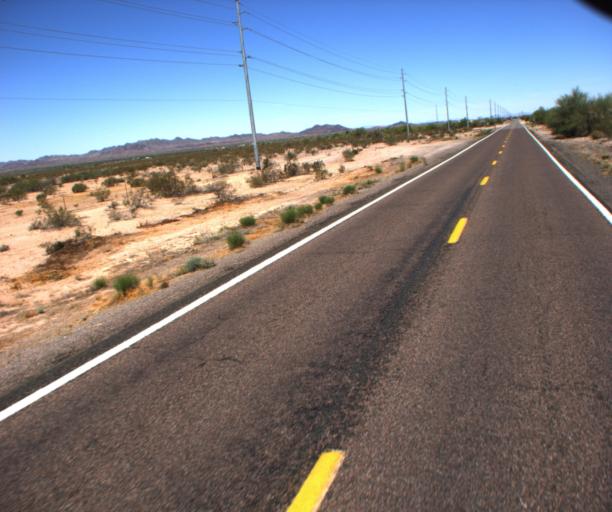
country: US
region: Arizona
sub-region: La Paz County
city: Quartzsite
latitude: 33.8991
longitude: -113.9711
